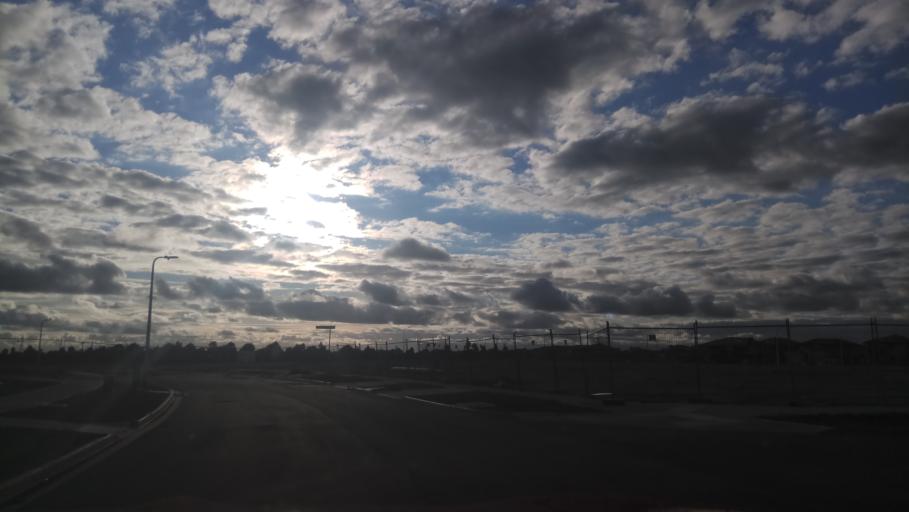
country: AU
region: Victoria
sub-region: Wyndham
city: Point Cook
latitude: -37.9122
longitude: 144.7484
